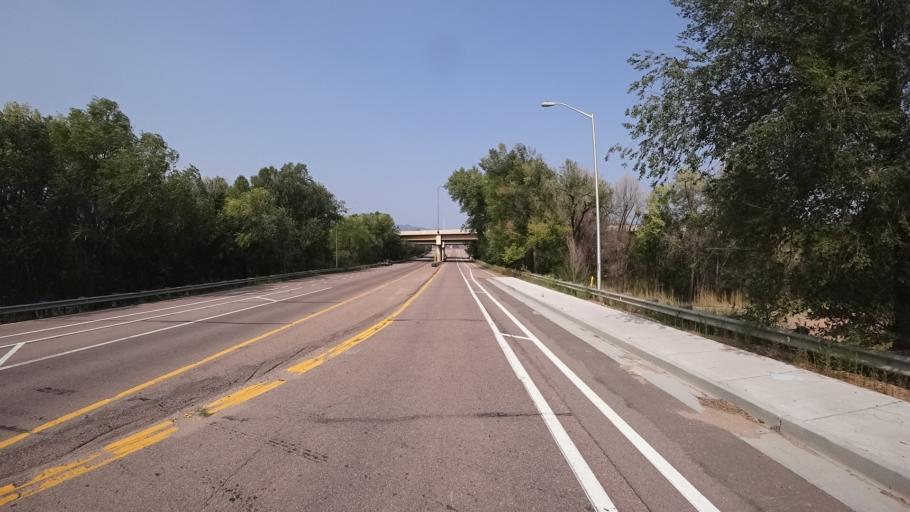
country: US
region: Colorado
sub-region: El Paso County
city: Colorado Springs
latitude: 38.8090
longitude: -104.7937
